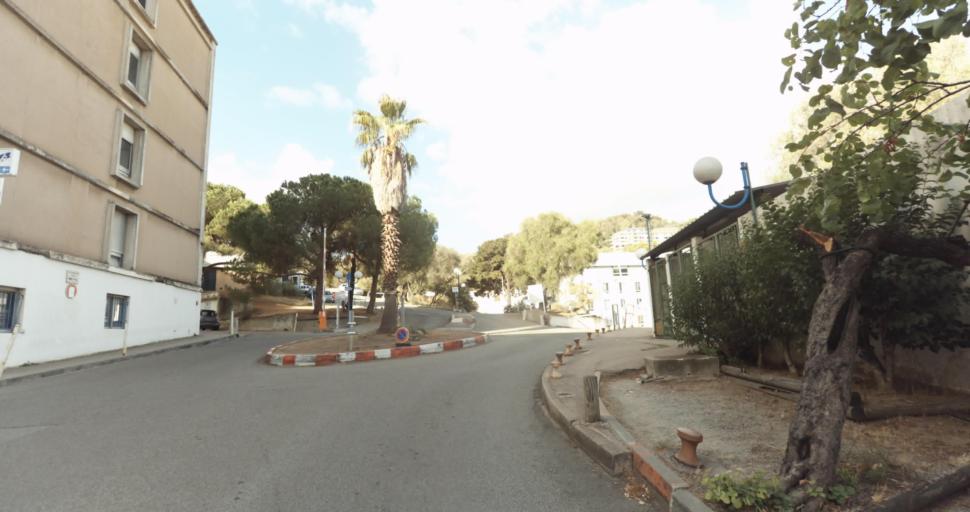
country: FR
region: Corsica
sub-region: Departement de la Corse-du-Sud
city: Ajaccio
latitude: 41.9235
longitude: 8.7339
